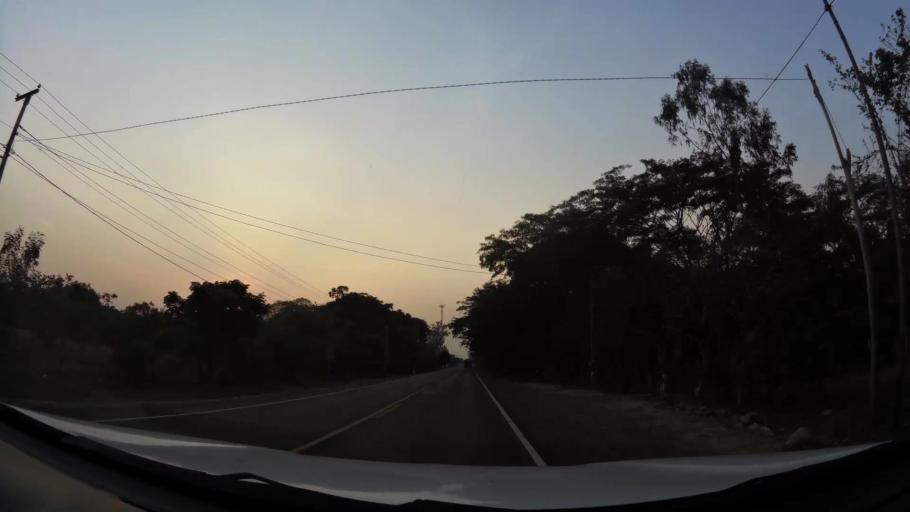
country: NI
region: Leon
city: Leon
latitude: 12.3344
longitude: -86.8098
